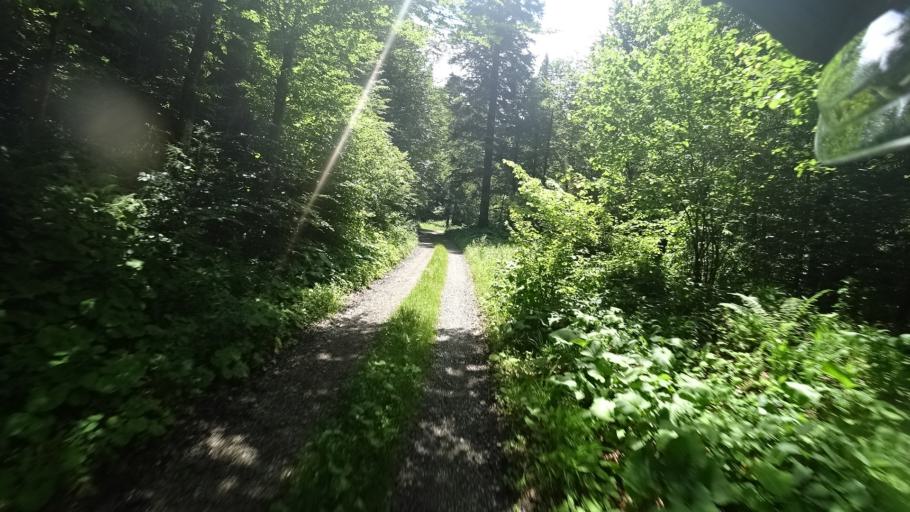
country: SI
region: Osilnica
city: Osilnica
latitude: 45.4720
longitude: 14.7281
